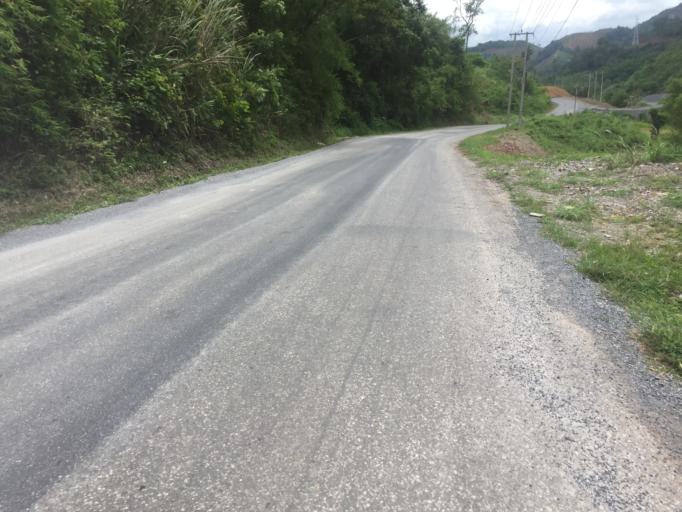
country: LA
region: Oudomxai
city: Muang Xay
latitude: 20.7475
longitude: 102.0328
